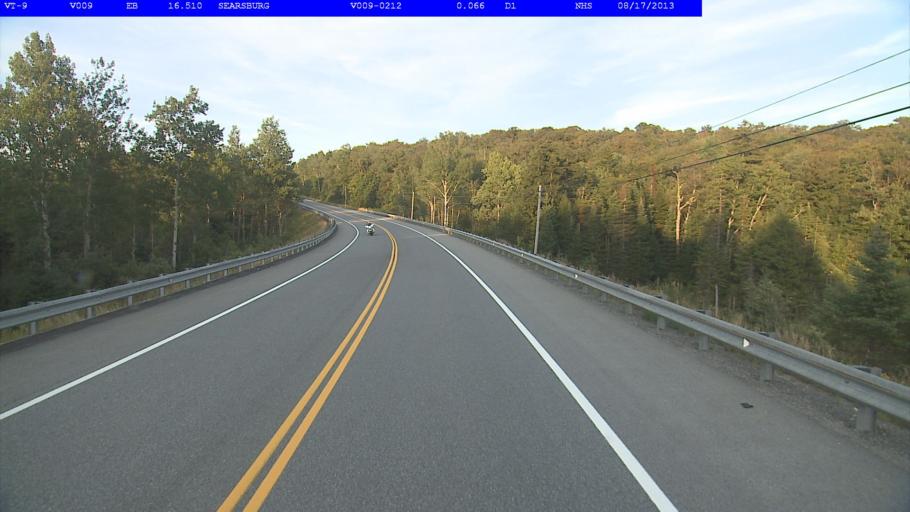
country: US
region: Vermont
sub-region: Bennington County
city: Bennington
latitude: 42.8895
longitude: -73.0090
